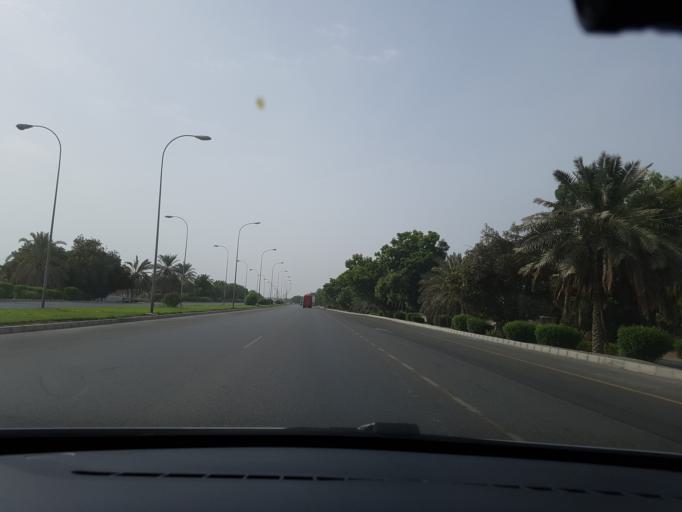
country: OM
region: Al Batinah
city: Al Sohar
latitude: 24.3681
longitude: 56.7060
